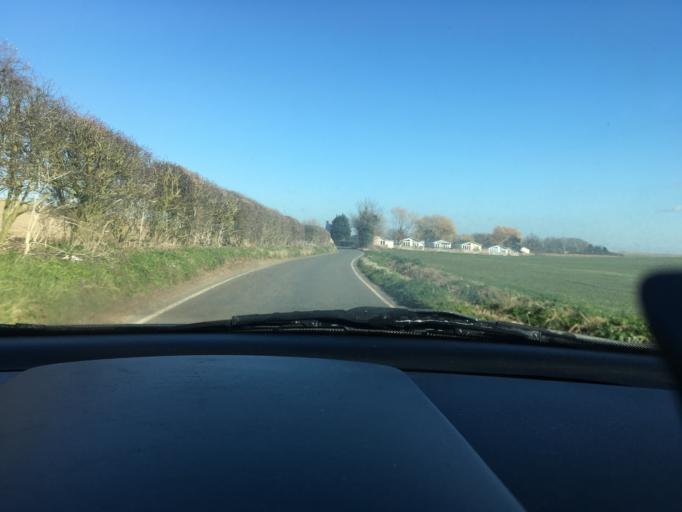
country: GB
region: England
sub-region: Kent
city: Herne Bay
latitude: 51.3745
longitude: 1.1903
